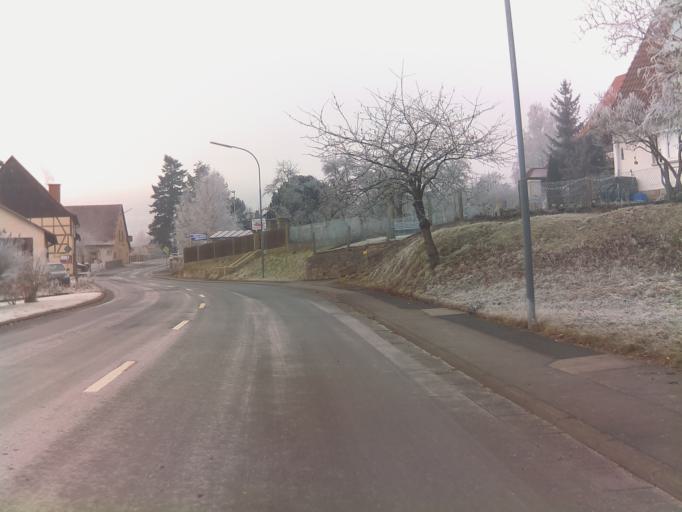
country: DE
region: Bavaria
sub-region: Regierungsbezirk Unterfranken
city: Bischofsheim an der Rhon
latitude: 50.3981
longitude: 10.0037
